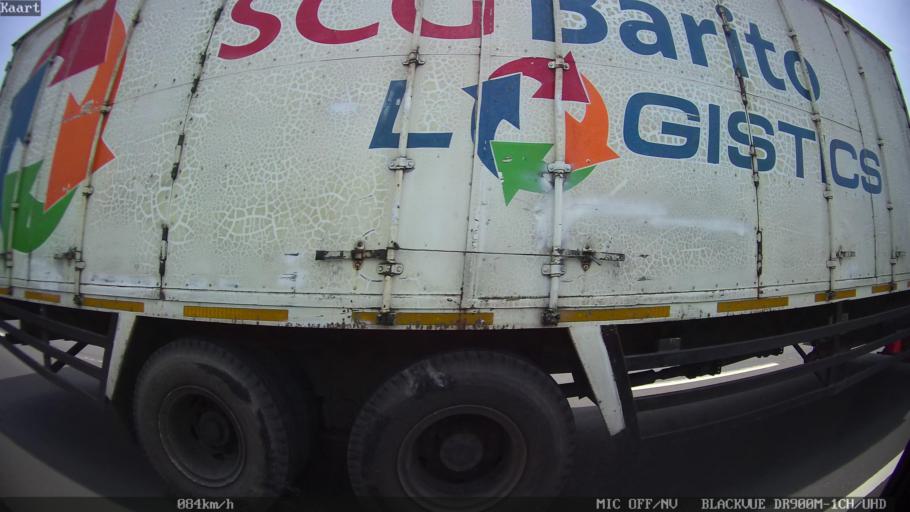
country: ID
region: West Java
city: Kresek
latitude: -6.1903
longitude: 106.4120
